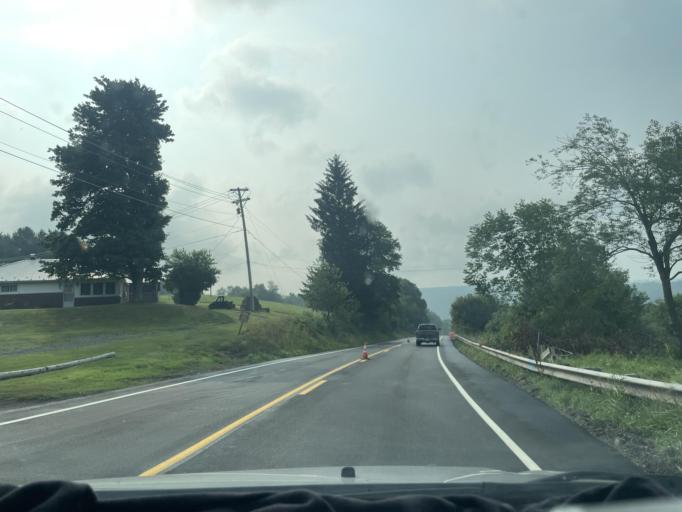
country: US
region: Maryland
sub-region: Garrett County
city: Mountain Lake Park
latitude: 39.2922
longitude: -79.3551
